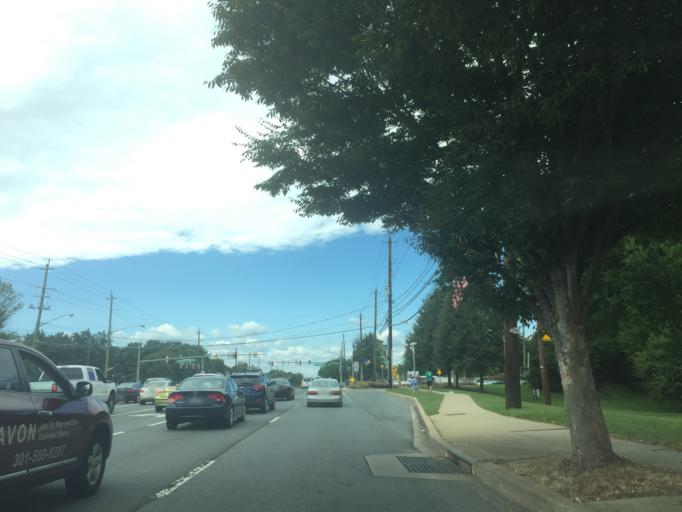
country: US
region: Maryland
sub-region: Montgomery County
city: Gaithersburg
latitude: 39.1518
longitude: -77.2109
